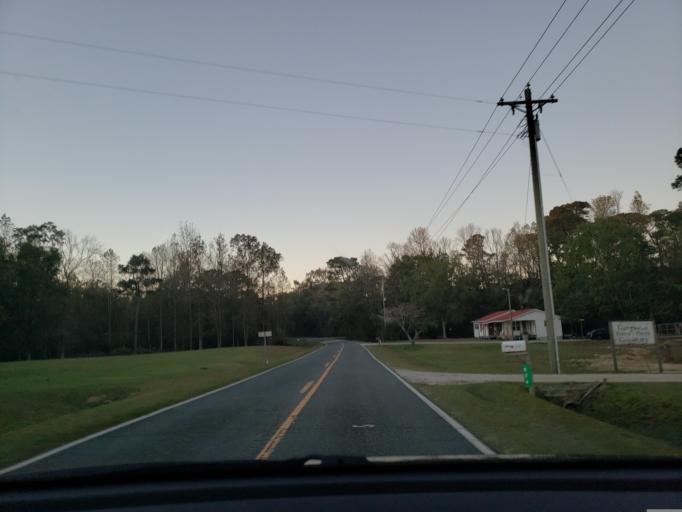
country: US
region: North Carolina
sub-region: Onslow County
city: Richlands
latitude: 34.7560
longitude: -77.6552
